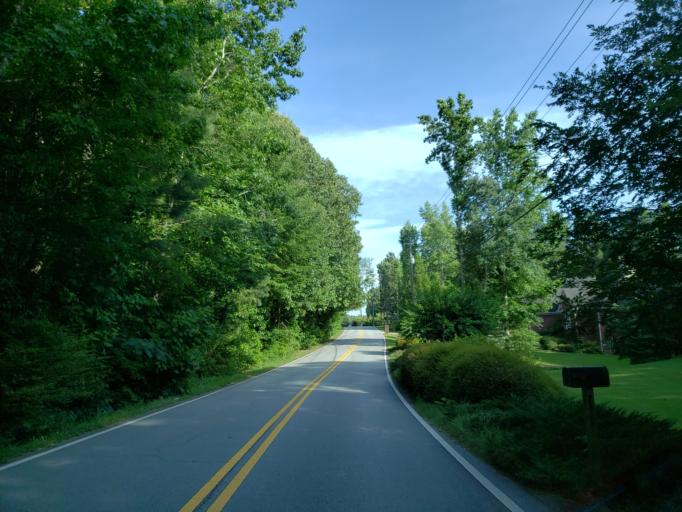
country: US
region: Georgia
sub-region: Paulding County
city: Hiram
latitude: 33.9169
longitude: -84.7189
